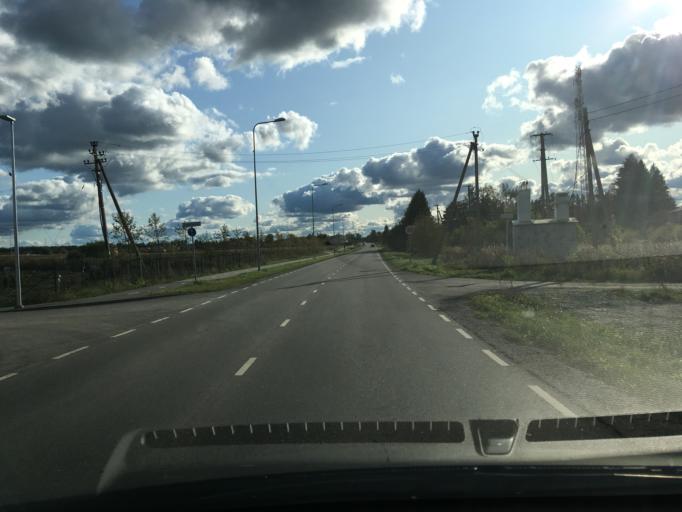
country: EE
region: Harju
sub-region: Joelaehtme vald
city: Loo
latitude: 59.4095
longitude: 24.9472
